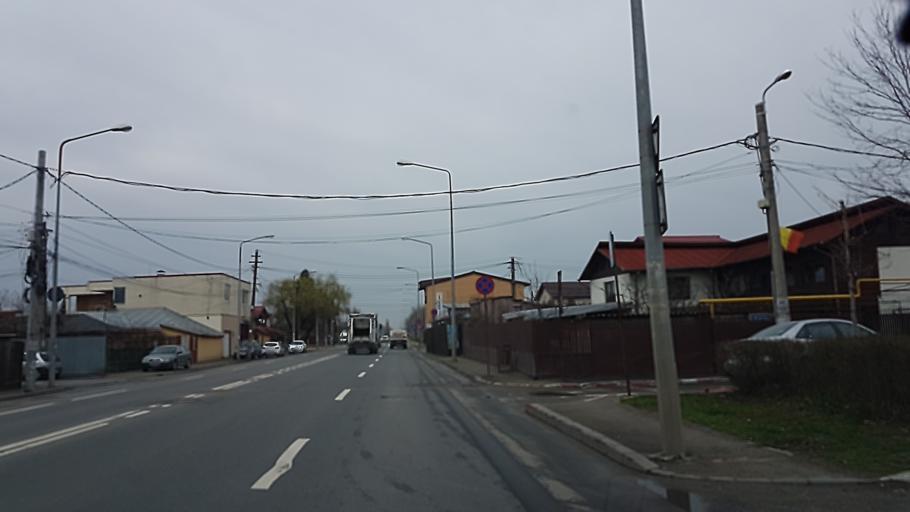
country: RO
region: Ilfov
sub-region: Comuna Glina
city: Catelu
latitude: 44.4284
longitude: 26.2168
